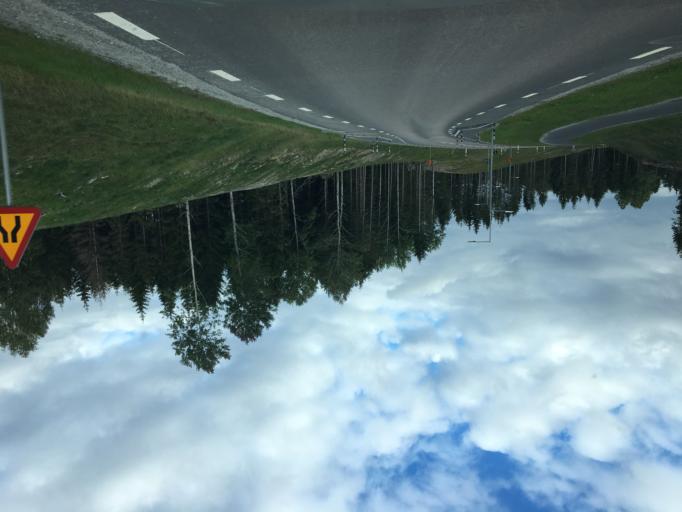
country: SE
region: Vaestmanland
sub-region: Vasteras
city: Vasteras
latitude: 59.5521
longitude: 16.6805
